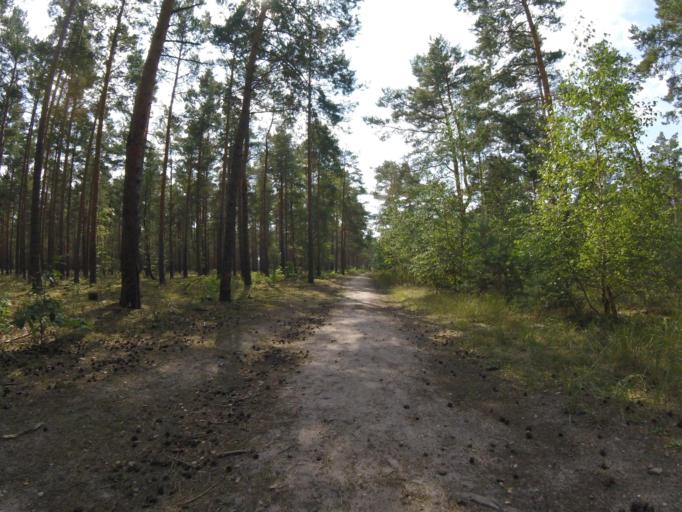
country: DE
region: Brandenburg
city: Bestensee
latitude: 52.2786
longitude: 13.6653
